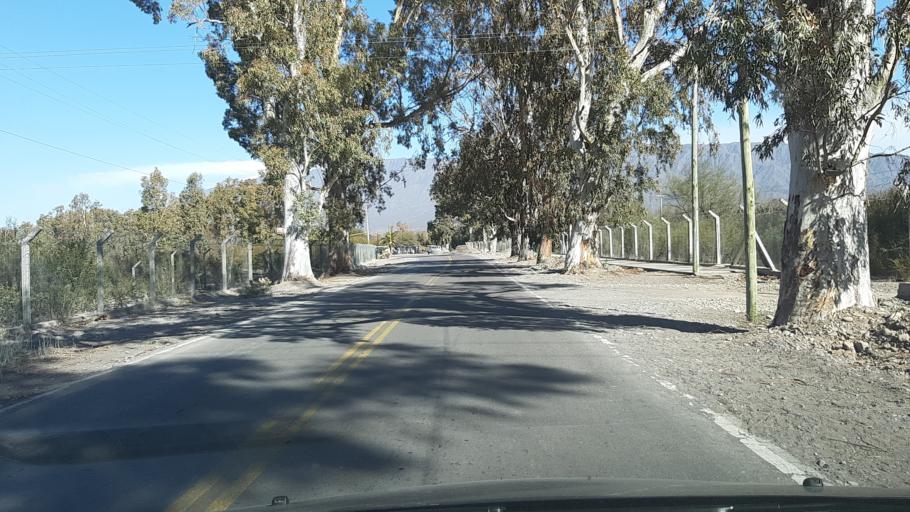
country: AR
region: San Juan
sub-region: Departamento de Zonda
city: Zonda
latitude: -31.5456
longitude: -68.7182
